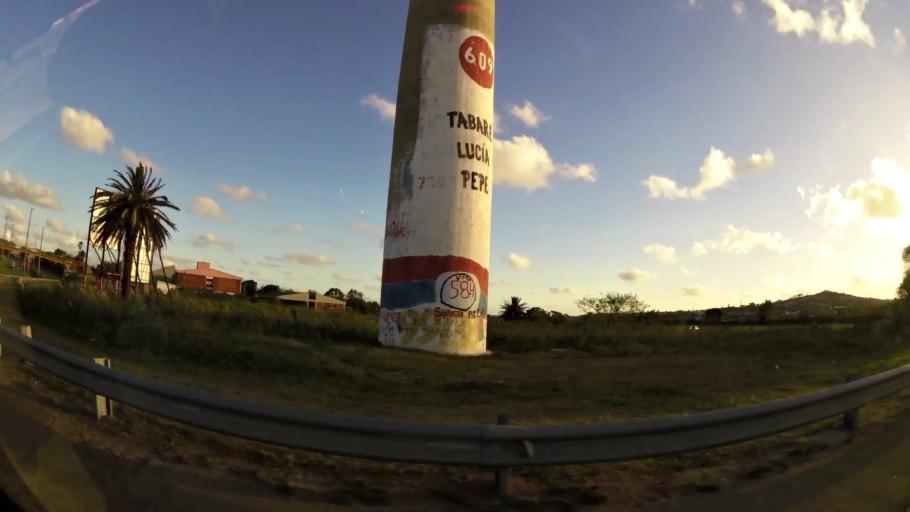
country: UY
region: Montevideo
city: Montevideo
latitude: -34.8716
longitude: -56.2414
